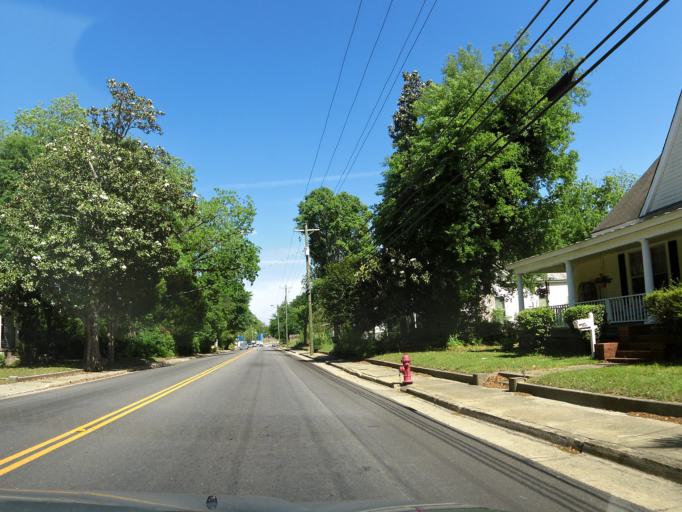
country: US
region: South Carolina
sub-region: Barnwell County
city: Williston
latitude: 33.4031
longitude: -81.4298
